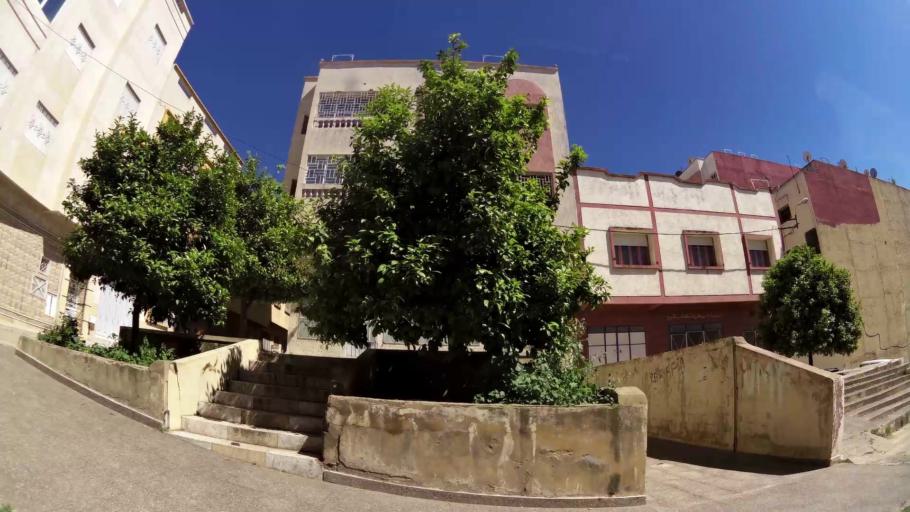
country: MA
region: Meknes-Tafilalet
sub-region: Meknes
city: Meknes
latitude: 33.8881
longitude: -5.5762
